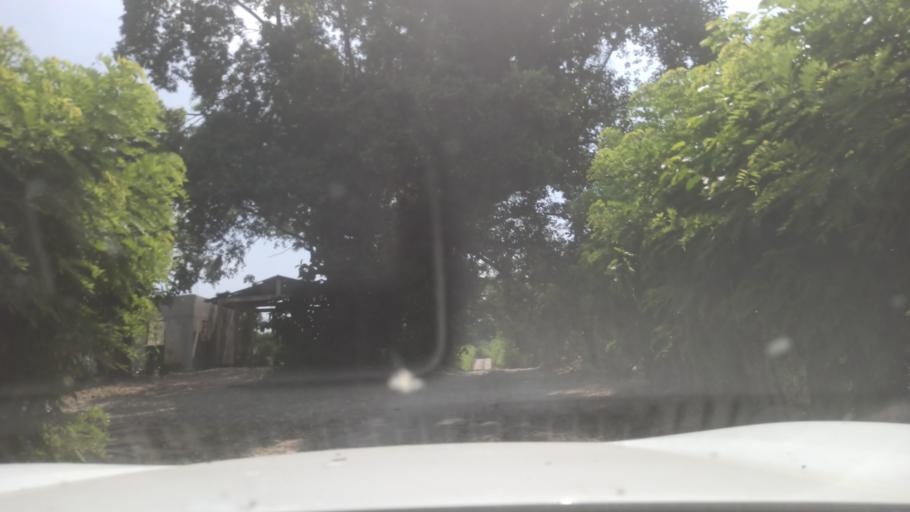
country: MX
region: Veracruz
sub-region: Atzalan
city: Colonias Pedernales
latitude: 20.0404
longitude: -97.0053
